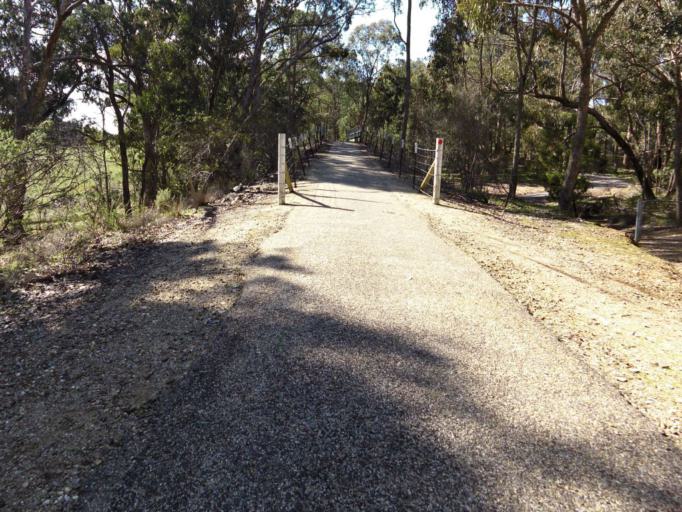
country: AU
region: Victoria
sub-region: Wangaratta
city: Wangaratta
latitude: -36.4032
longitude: 146.6391
